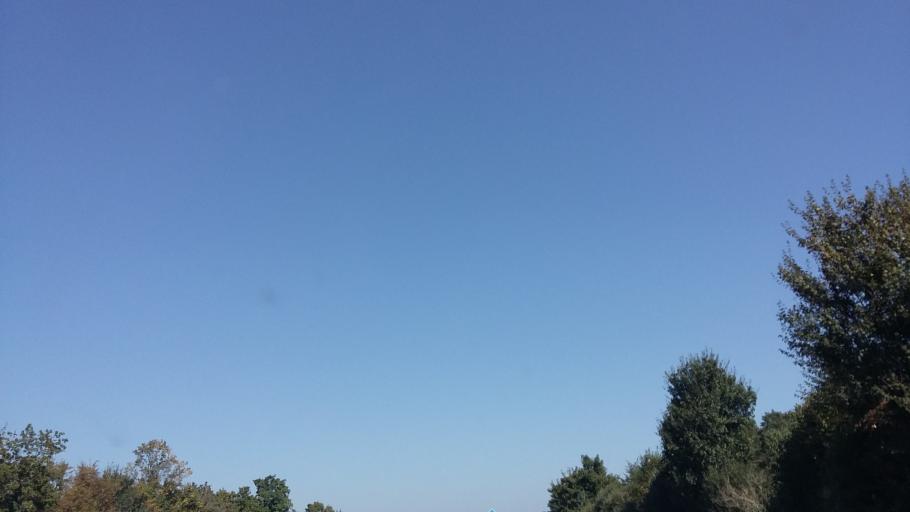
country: DE
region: Bavaria
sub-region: Swabia
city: Kleinaitingen
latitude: 48.1958
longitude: 10.8516
